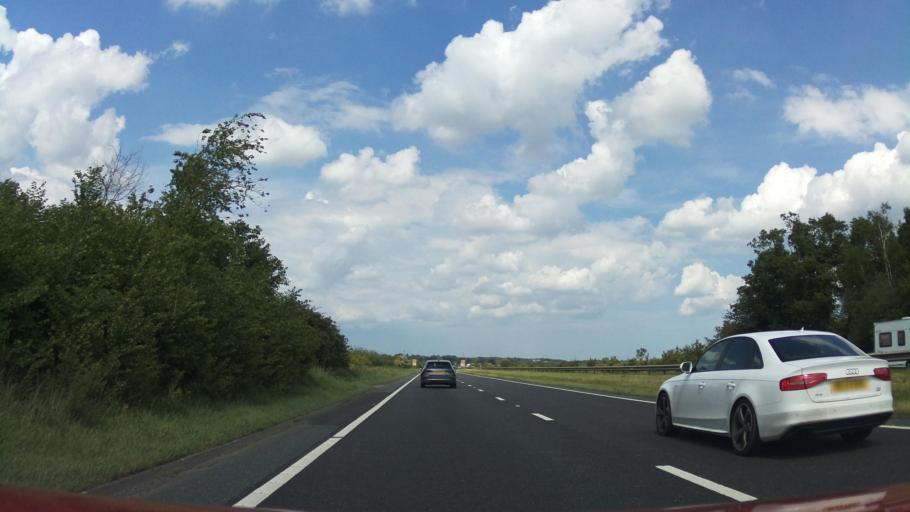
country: GB
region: England
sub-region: Stockton-on-Tees
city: Yarm
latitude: 54.4437
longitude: -1.3236
